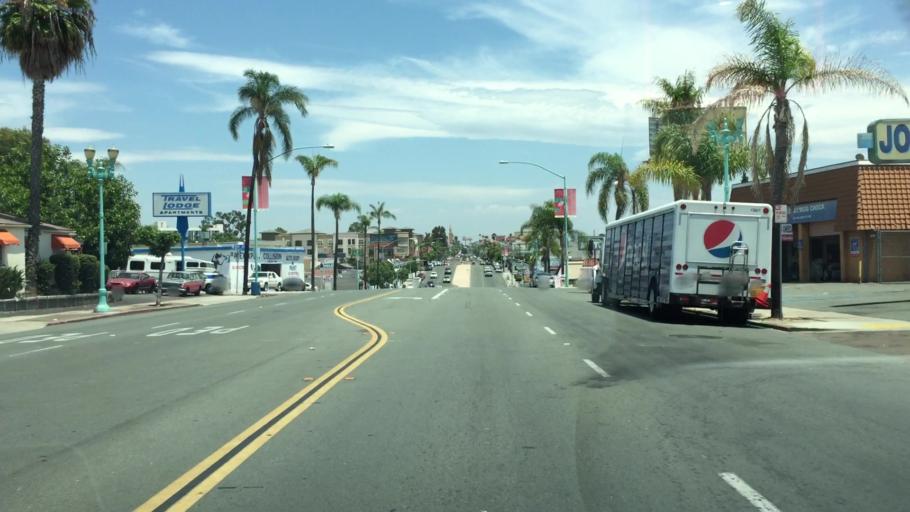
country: US
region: California
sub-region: San Diego County
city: Lemon Grove
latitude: 32.7569
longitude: -117.0854
